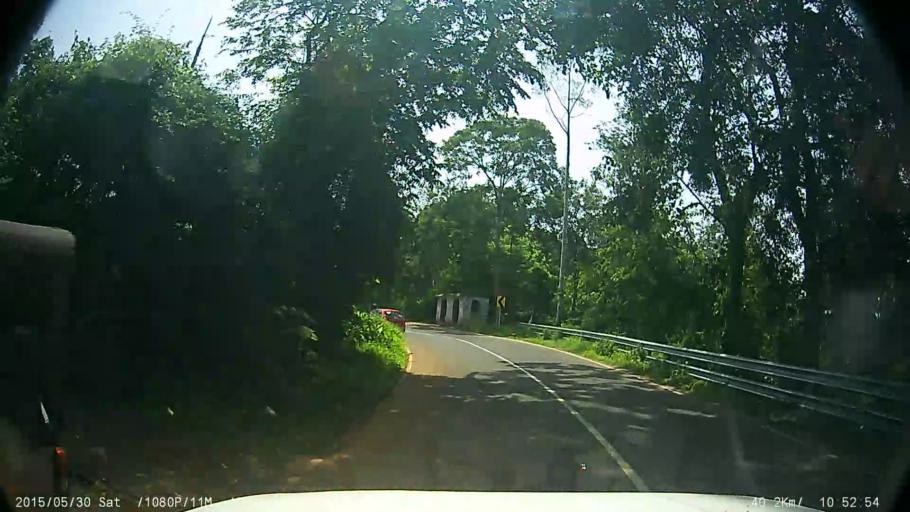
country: IN
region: Kerala
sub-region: Wayanad
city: Kalpetta
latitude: 11.6556
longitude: 76.0875
